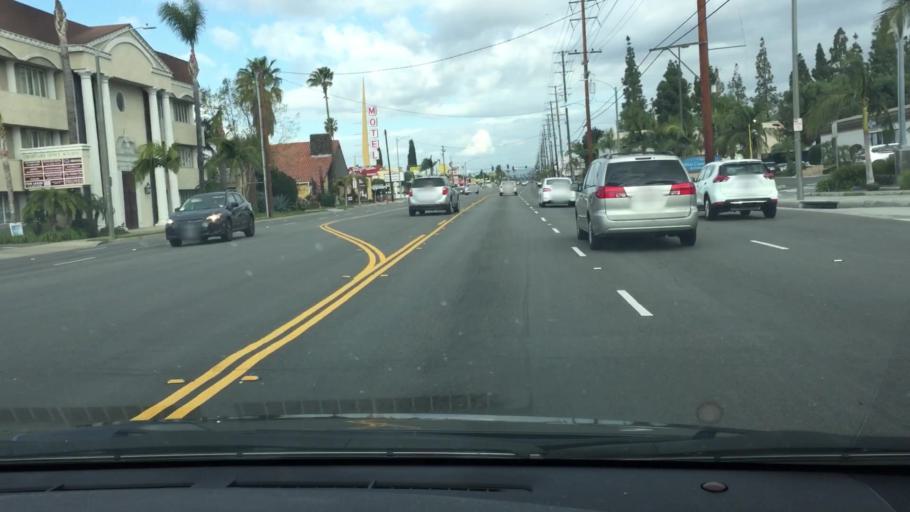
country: US
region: California
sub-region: Orange County
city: Orange
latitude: 33.7887
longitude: -117.8357
